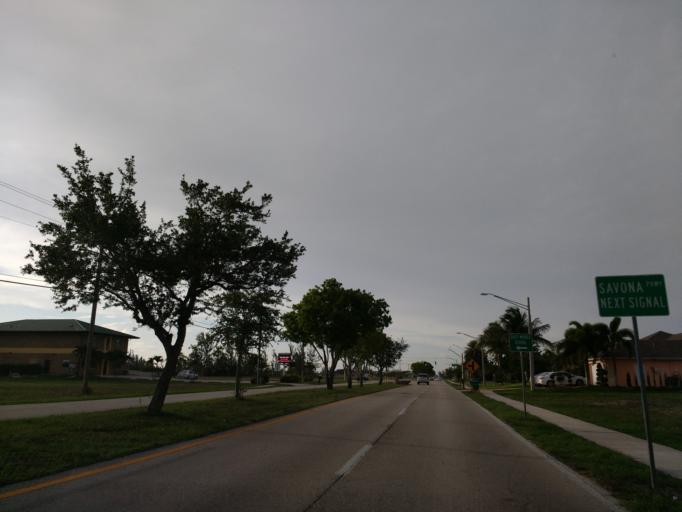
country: US
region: Florida
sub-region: Lee County
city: Cape Coral
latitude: 26.5823
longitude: -82.0068
